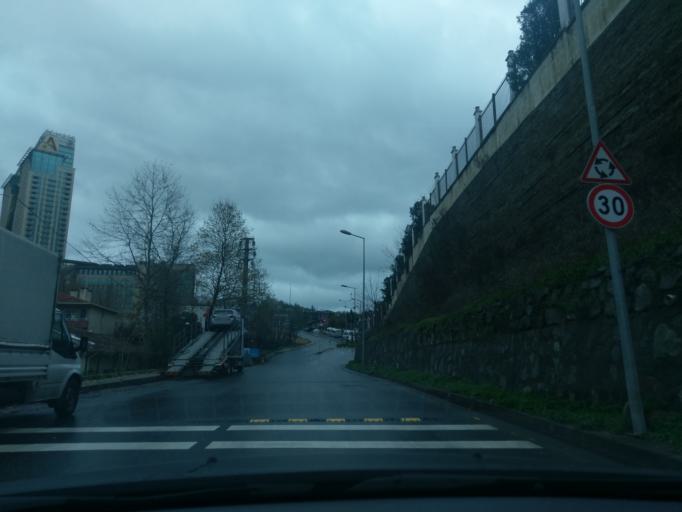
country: TR
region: Istanbul
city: Sisli
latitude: 41.1137
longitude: 29.0140
